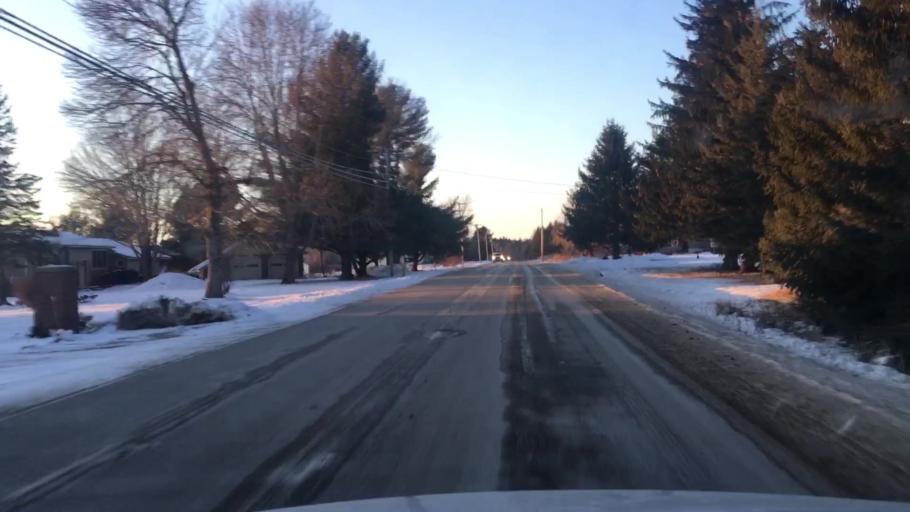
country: US
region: Maine
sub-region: Penobscot County
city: Brewer
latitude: 44.7322
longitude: -68.7606
